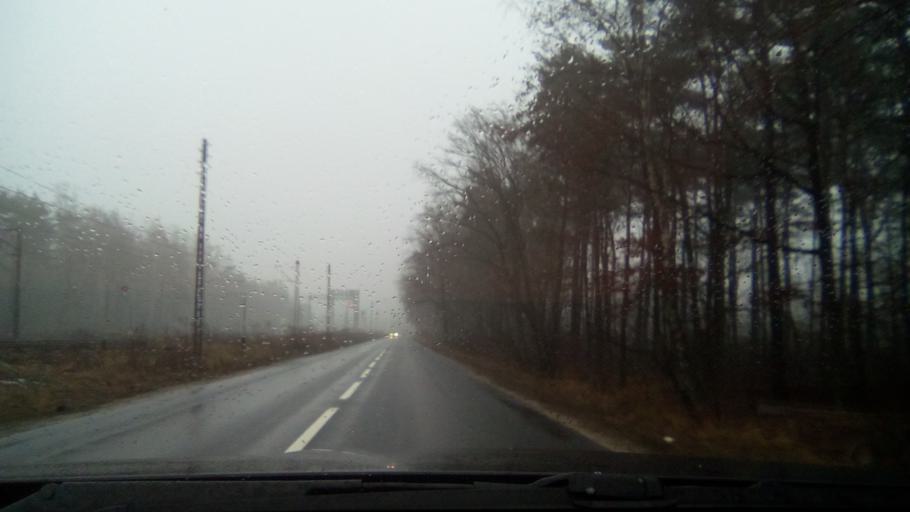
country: PL
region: Greater Poland Voivodeship
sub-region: Powiat poznanski
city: Swarzedz
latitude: 52.3965
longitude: 17.0407
